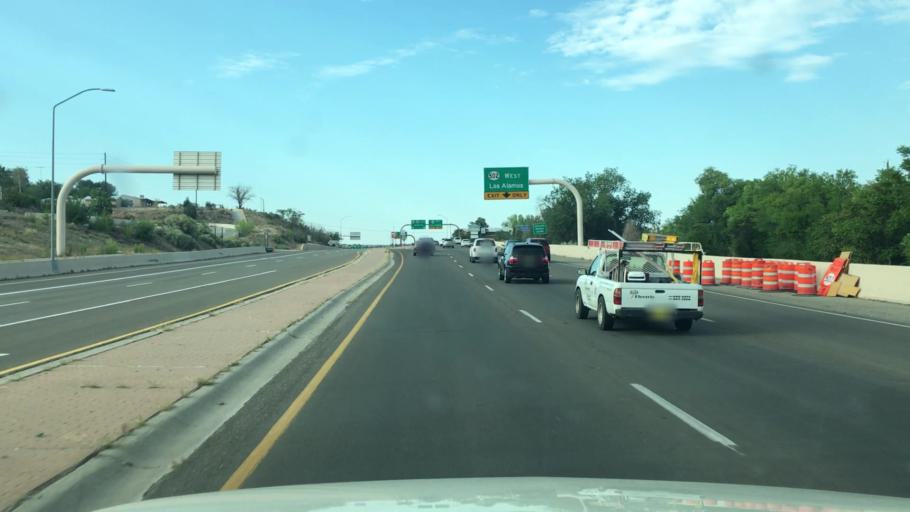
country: US
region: New Mexico
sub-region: Santa Fe County
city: Pojoaque
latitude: 35.8963
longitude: -106.0217
